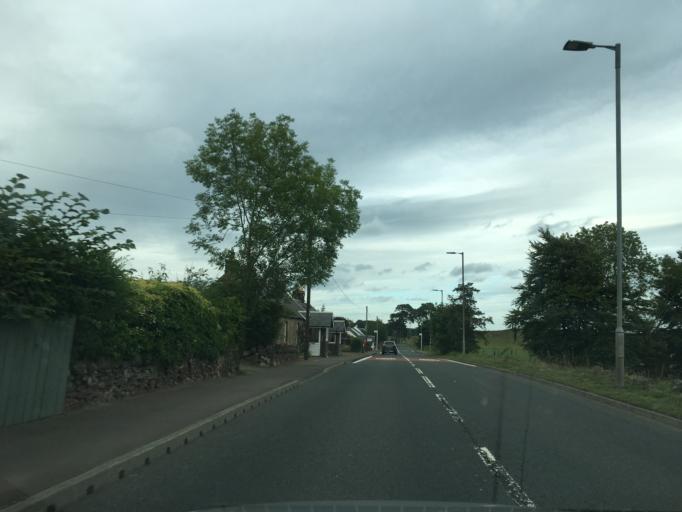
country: GB
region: Scotland
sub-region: The Scottish Borders
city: West Linton
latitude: 55.7045
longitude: -3.4271
